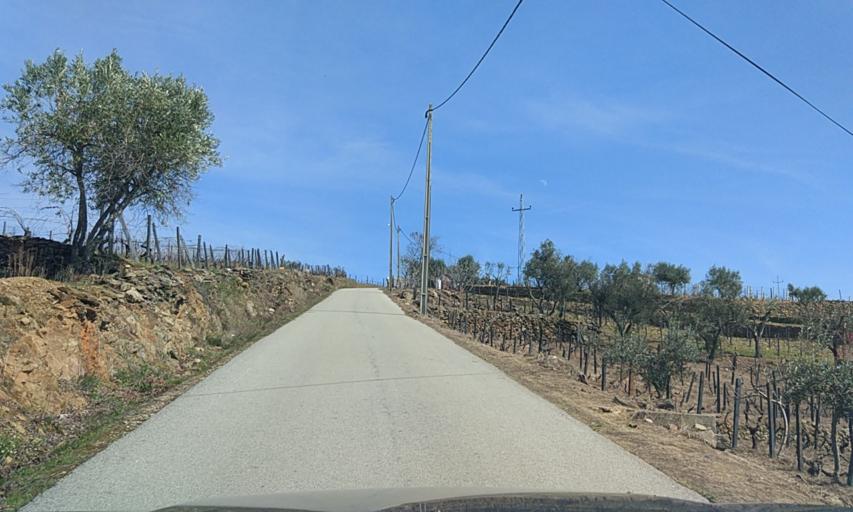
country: PT
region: Vila Real
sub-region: Sabrosa
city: Sabrosa
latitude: 41.2964
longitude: -7.5447
